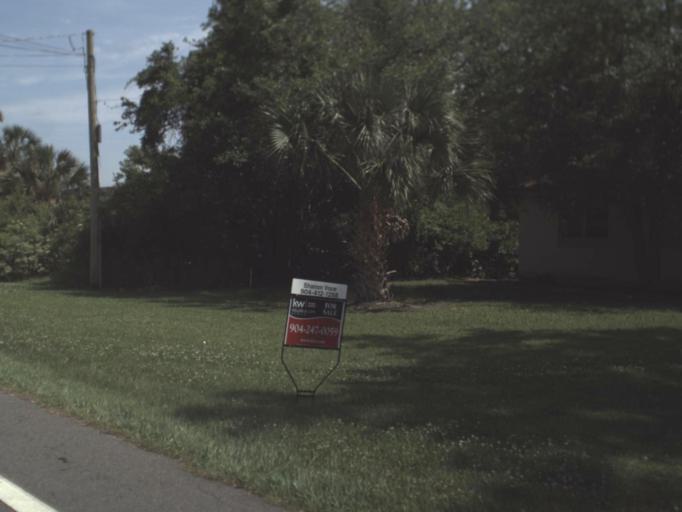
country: US
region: Florida
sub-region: Duval County
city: Atlantic Beach
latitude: 30.4132
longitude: -81.5219
